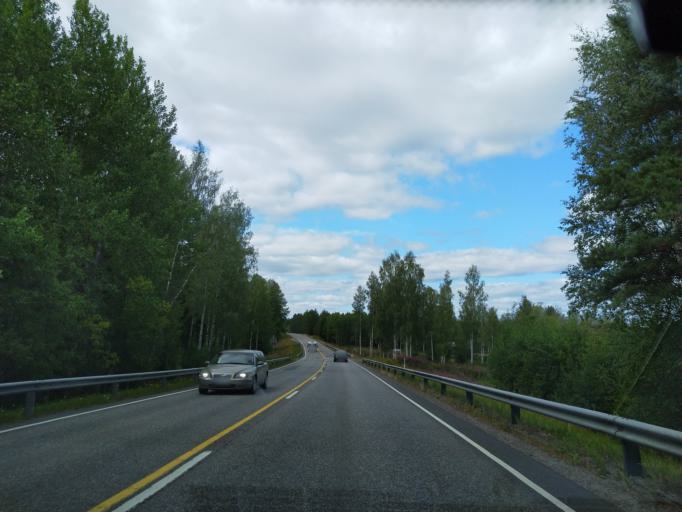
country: FI
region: Haeme
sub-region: Riihimaeki
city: Loppi
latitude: 60.7477
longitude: 24.3373
